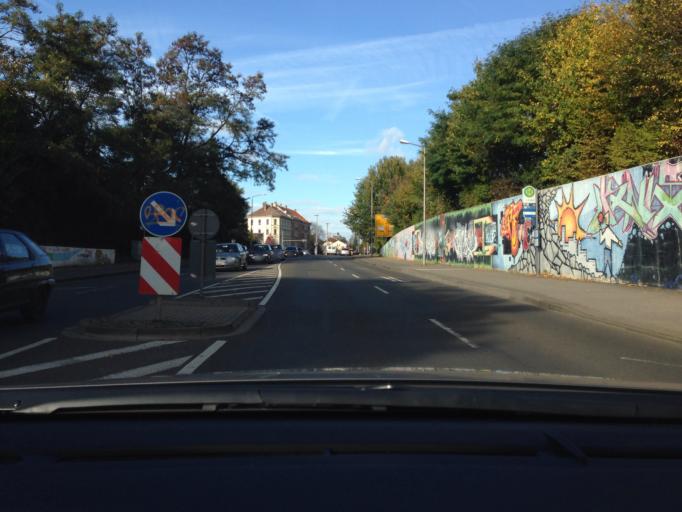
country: DE
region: Saxony
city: Taucha
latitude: 51.3446
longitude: 12.4452
